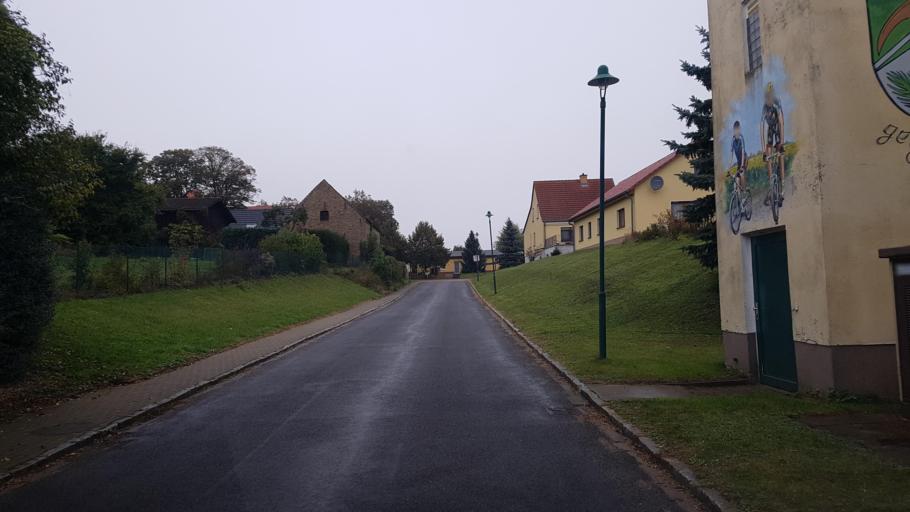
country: DE
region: Brandenburg
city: Furstenwalde
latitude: 52.4329
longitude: 14.0168
